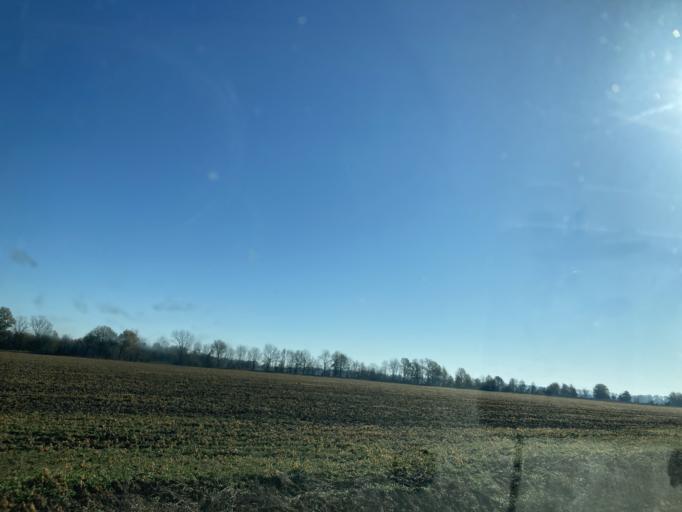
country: US
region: Mississippi
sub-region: Sharkey County
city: Rolling Fork
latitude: 32.8994
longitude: -90.6598
